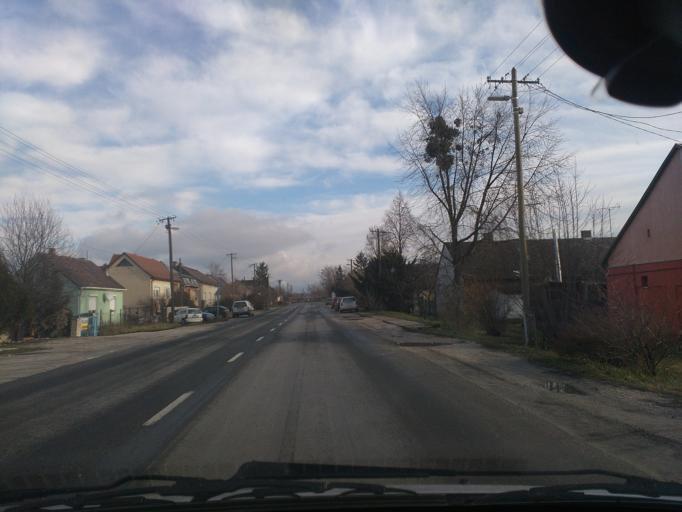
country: HU
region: Komarom-Esztergom
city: Tokod
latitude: 47.7360
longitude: 18.6724
